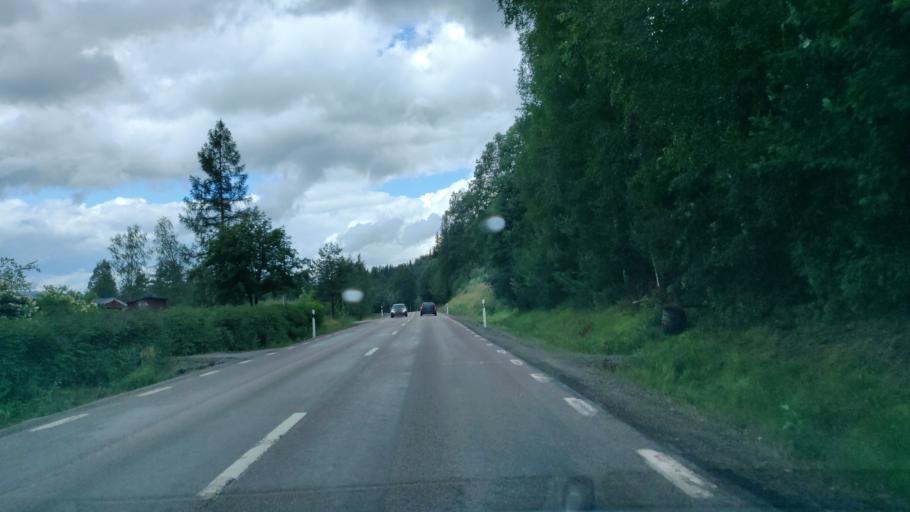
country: SE
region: Vaermland
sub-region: Torsby Kommun
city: Torsby
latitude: 60.5943
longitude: 13.0729
